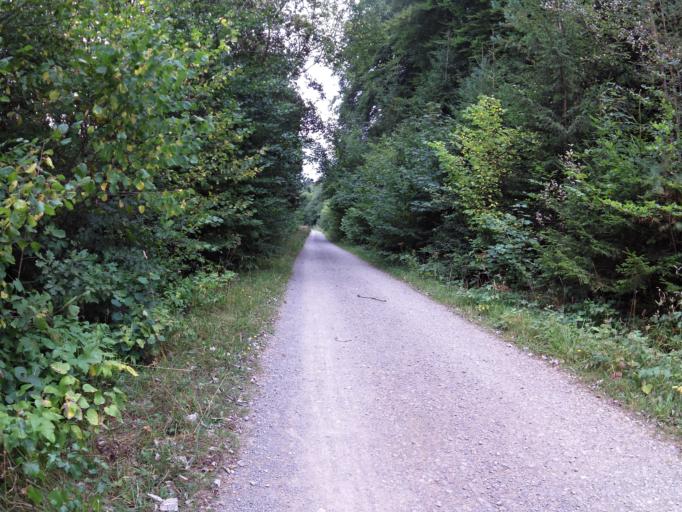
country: DE
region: North Rhine-Westphalia
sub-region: Regierungsbezirk Koln
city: Nettersheim
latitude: 50.5121
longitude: 6.6038
